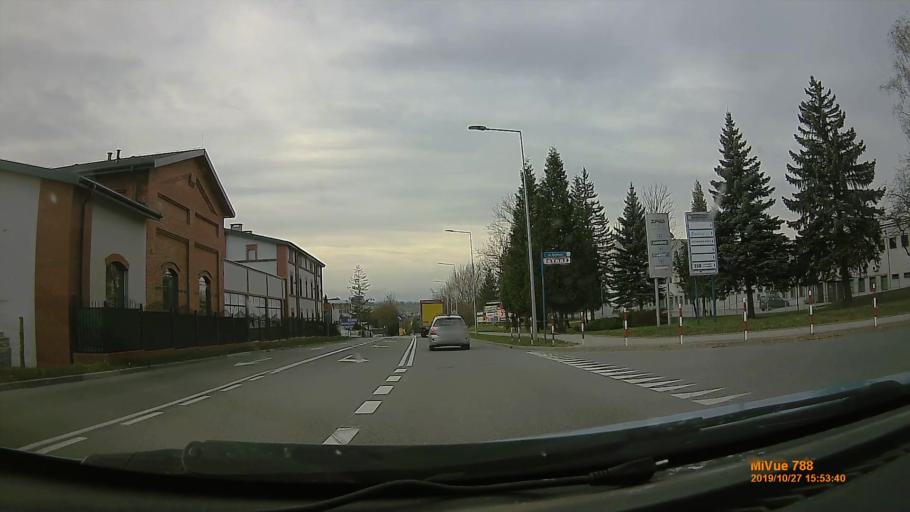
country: PL
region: Lower Silesian Voivodeship
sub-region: Powiat klodzki
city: Bozkow
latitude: 50.5385
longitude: 16.5644
